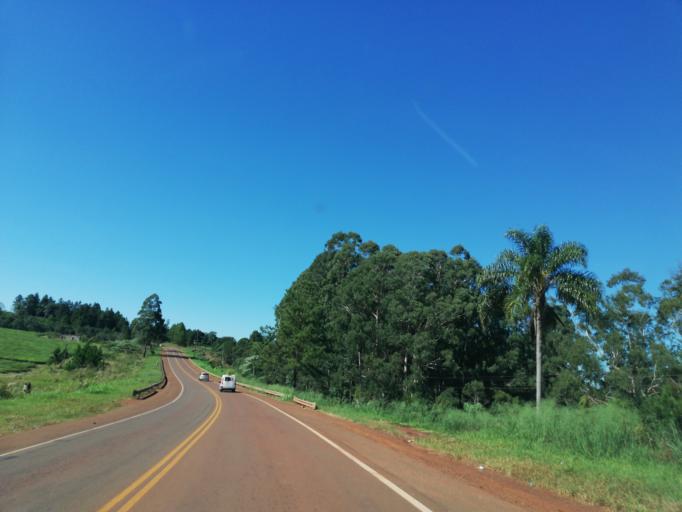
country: AR
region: Misiones
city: Dos de Mayo
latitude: -27.0461
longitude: -54.4371
